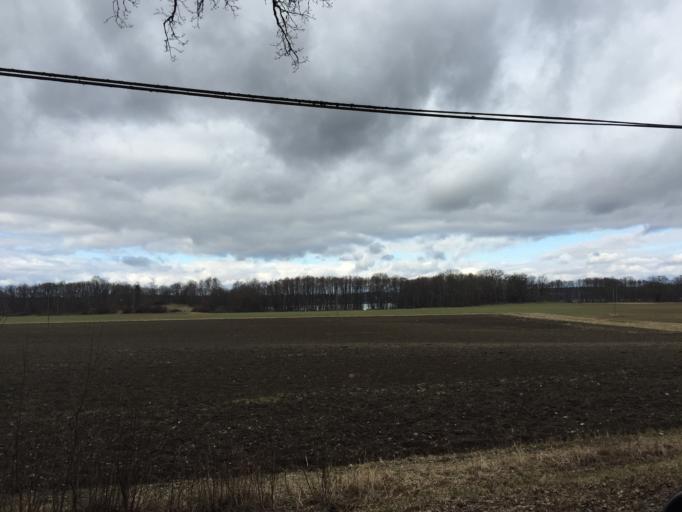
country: SE
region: Stockholm
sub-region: Botkyrka Kommun
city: Eriksberg
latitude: 59.2510
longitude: 17.7746
